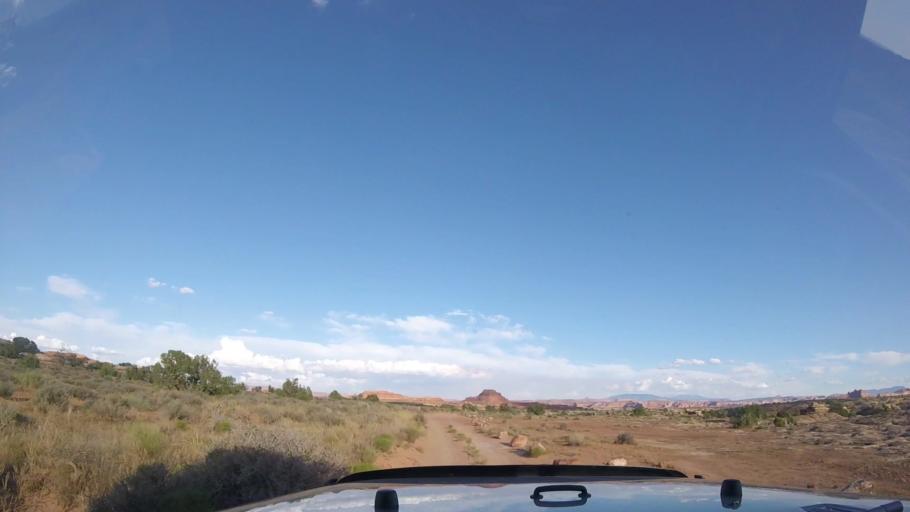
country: US
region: Utah
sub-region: Grand County
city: Moab
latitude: 38.1994
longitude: -109.7819
